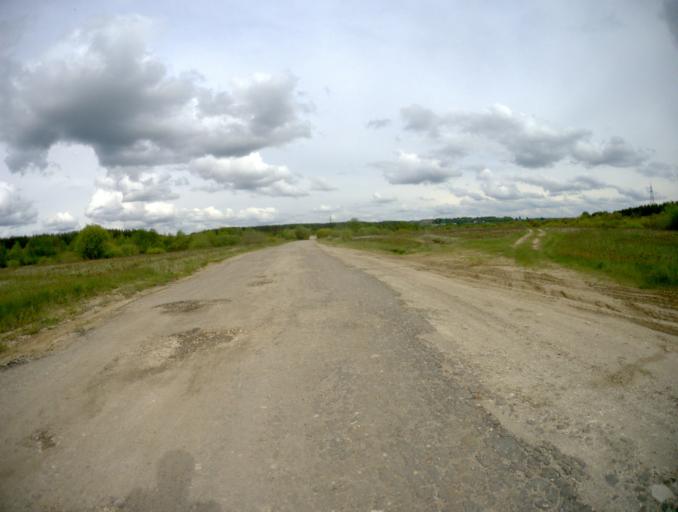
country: RU
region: Rjazan
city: Gus'-Zheleznyy
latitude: 55.0108
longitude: 41.1669
